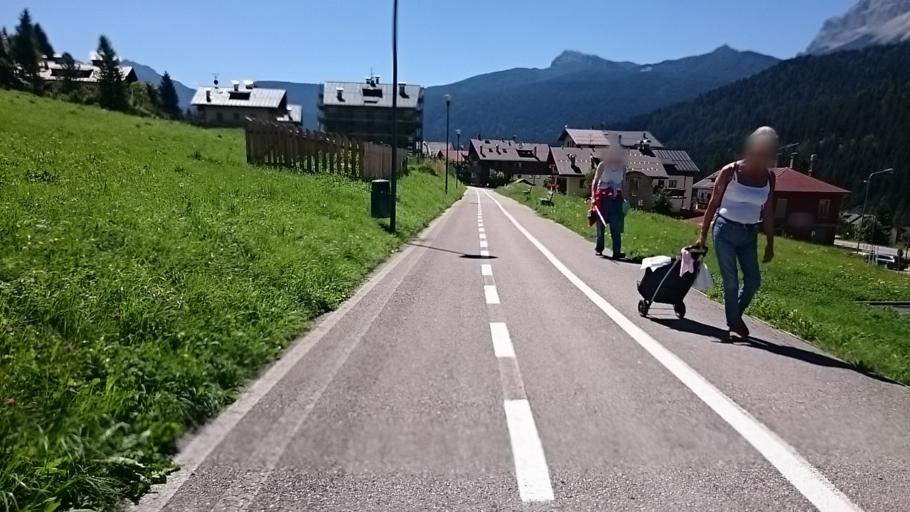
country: IT
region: Veneto
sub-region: Provincia di Belluno
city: San Vito
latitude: 46.4664
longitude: 12.2049
